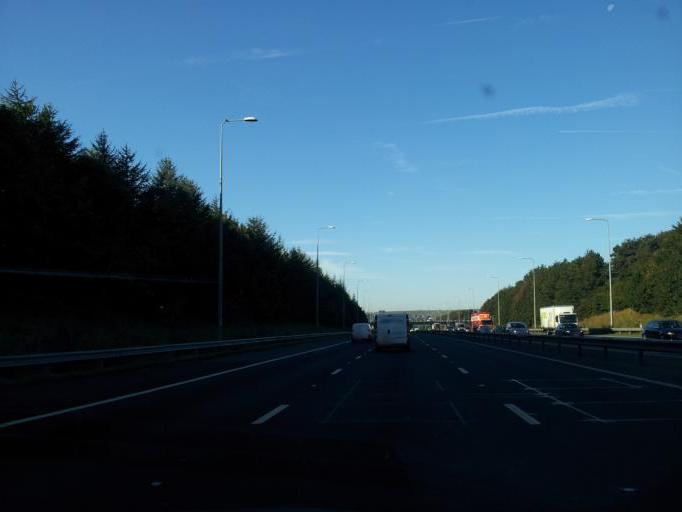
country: GB
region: England
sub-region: Calderdale
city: Elland
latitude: 53.6617
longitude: -1.8559
